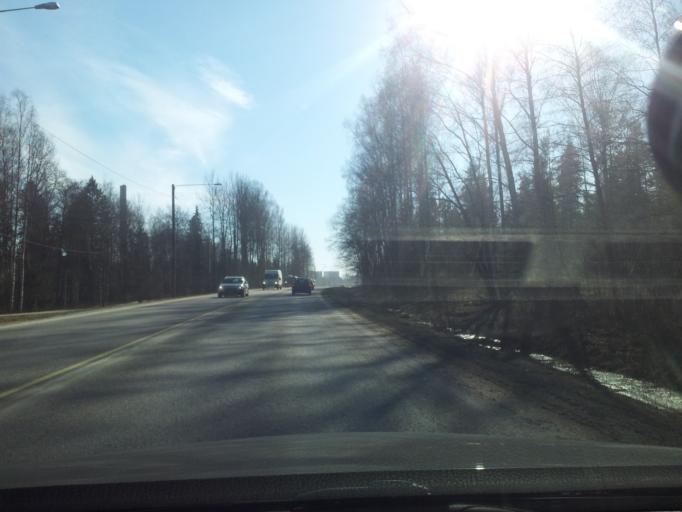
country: FI
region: Uusimaa
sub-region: Helsinki
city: Espoo
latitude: 60.1641
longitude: 24.6261
